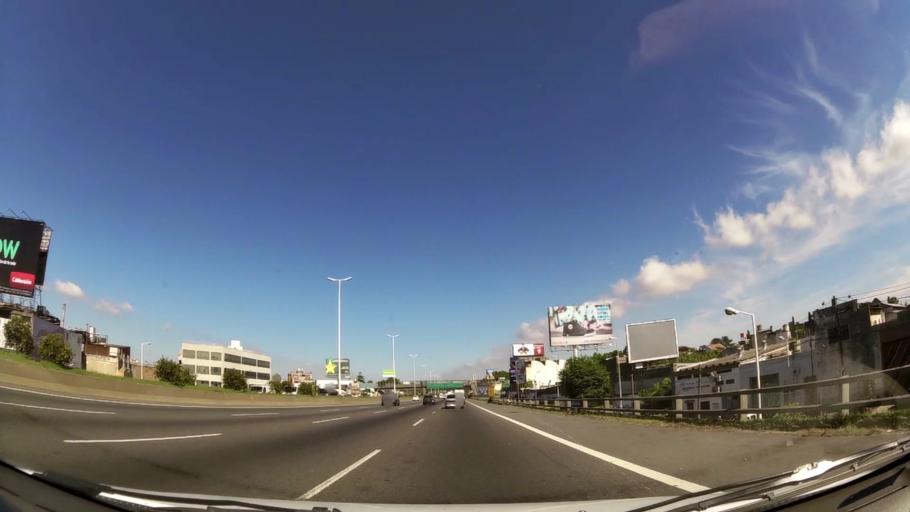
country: AR
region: Buenos Aires
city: Caseros
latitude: -34.6331
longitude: -58.5411
